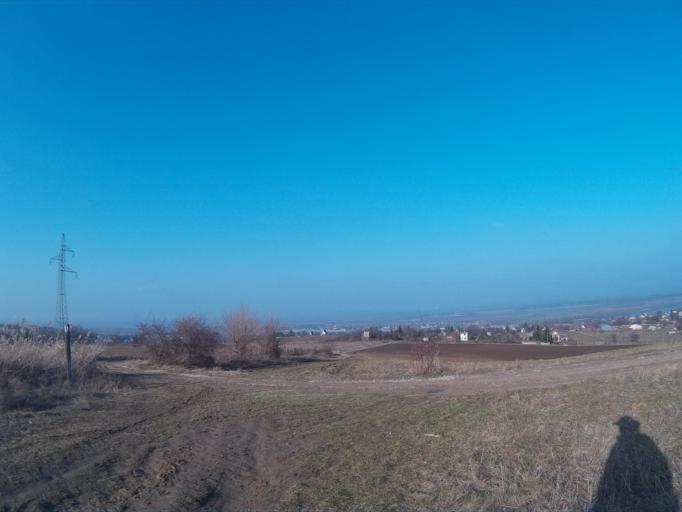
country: HU
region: Komarom-Esztergom
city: Labatlan
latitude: 47.7391
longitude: 18.4822
